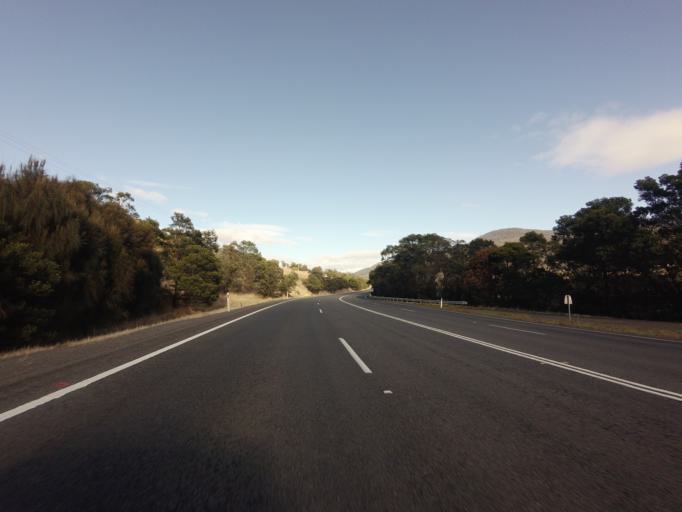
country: AU
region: Tasmania
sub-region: Glenorchy
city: Granton
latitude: -42.7527
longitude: 147.1694
